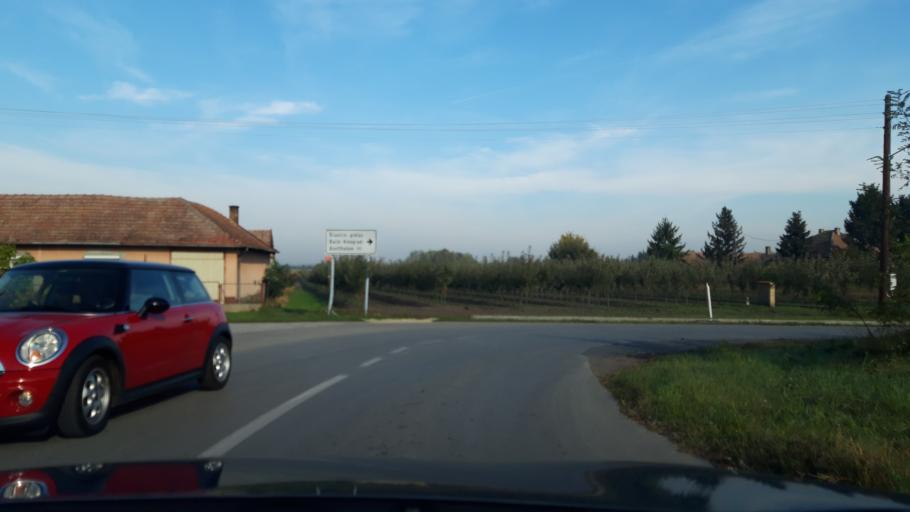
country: HU
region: Csongrad
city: Asotthalom
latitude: 46.1256
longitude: 19.8497
